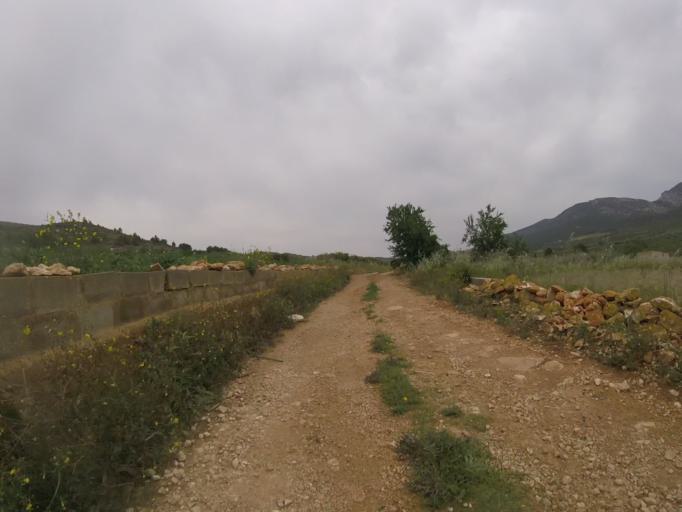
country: ES
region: Valencia
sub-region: Provincia de Castello
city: Alcala de Xivert
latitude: 40.2832
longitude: 0.2561
